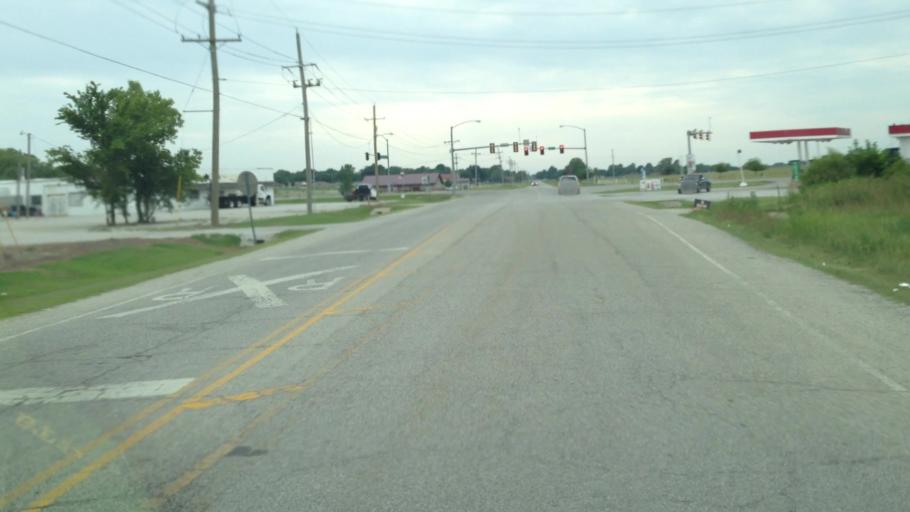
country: US
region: Oklahoma
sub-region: Craig County
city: Vinita
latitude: 36.6560
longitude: -95.1430
